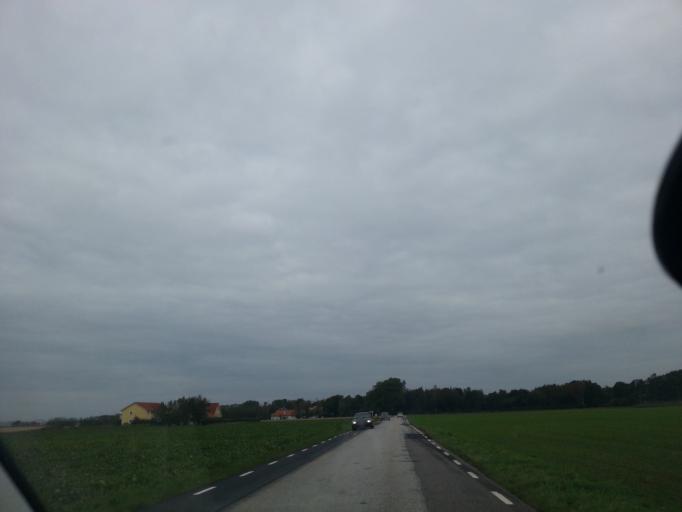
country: SE
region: Skane
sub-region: Landskrona
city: Asmundtorp
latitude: 55.8276
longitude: 12.9277
